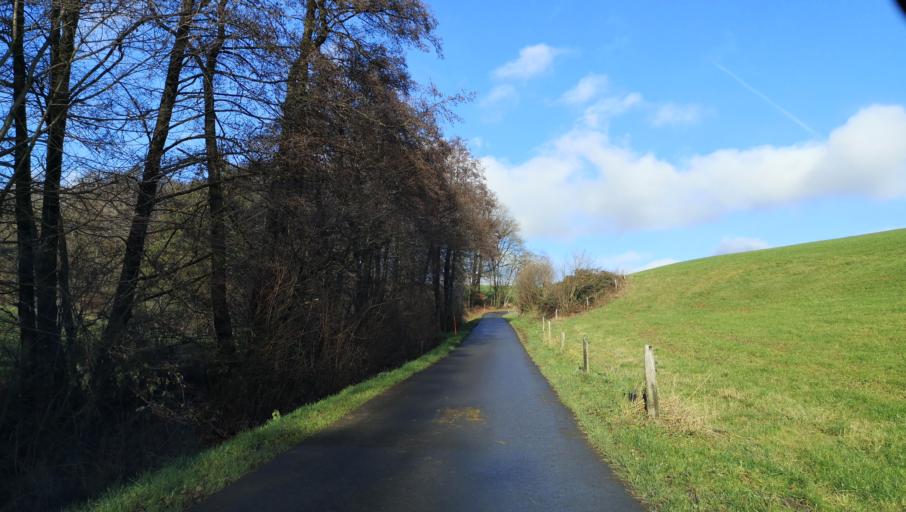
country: DE
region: North Rhine-Westphalia
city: Radevormwald
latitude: 51.1819
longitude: 7.4144
